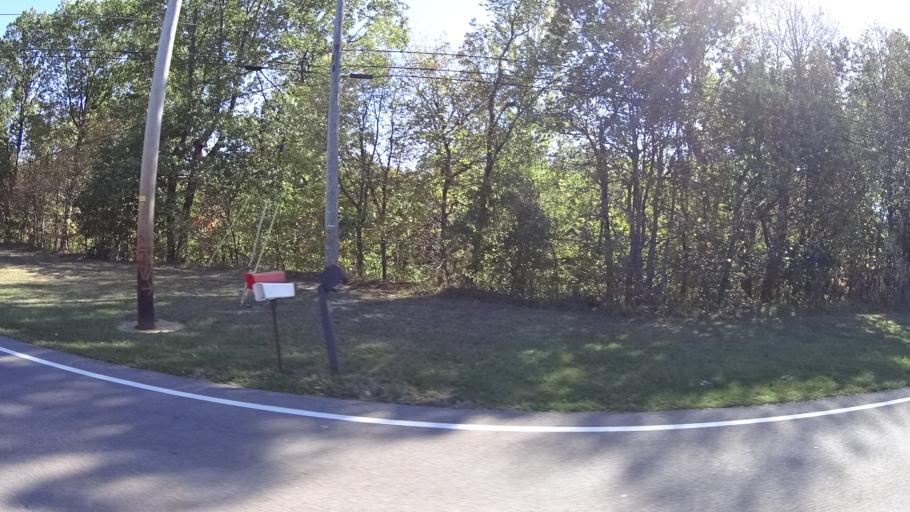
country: US
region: Ohio
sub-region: Lorain County
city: Amherst
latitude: 41.4139
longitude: -82.2291
